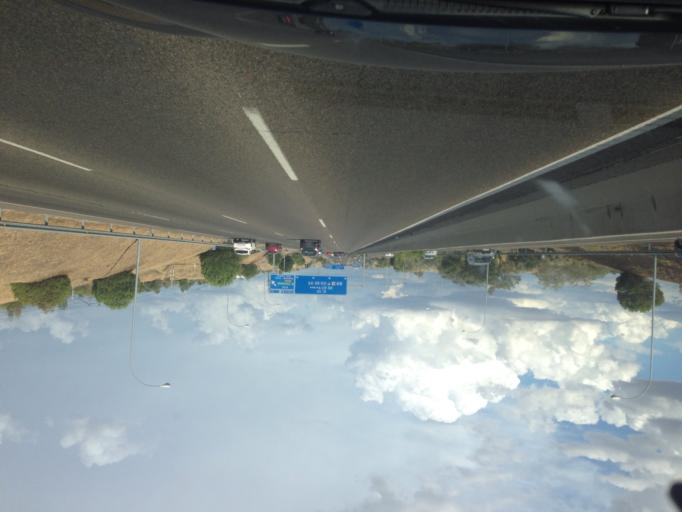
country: ES
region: Madrid
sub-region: Provincia de Madrid
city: Fuencarral-El Pardo
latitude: 40.5082
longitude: -3.7074
